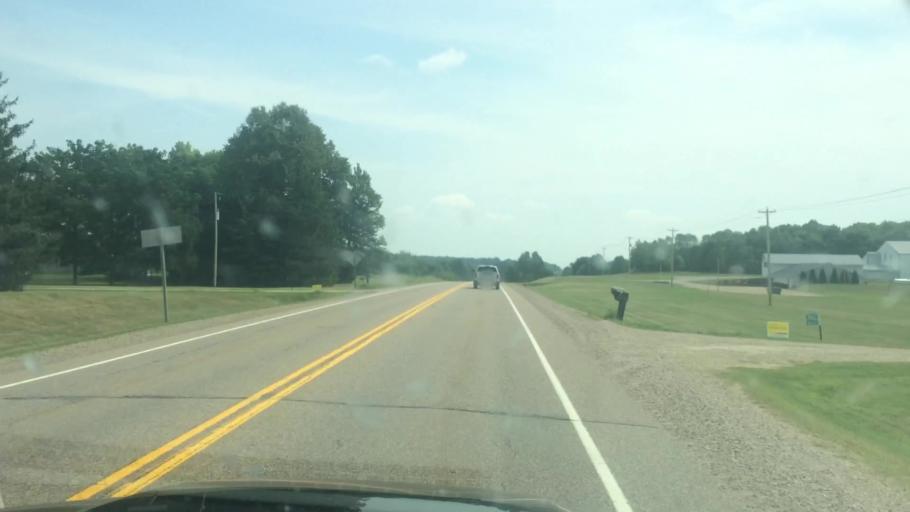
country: US
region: Wisconsin
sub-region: Langlade County
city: Antigo
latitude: 45.1687
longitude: -88.8761
